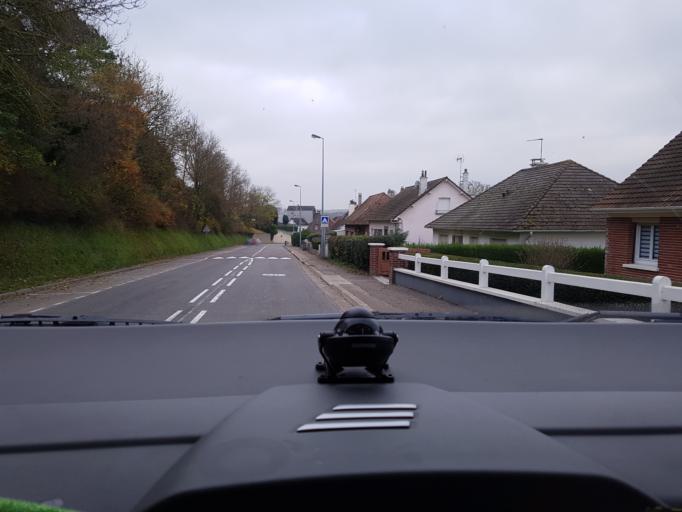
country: FR
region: Haute-Normandie
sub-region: Departement de la Seine-Maritime
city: Criel-sur-Mer
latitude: 50.0194
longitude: 1.3204
